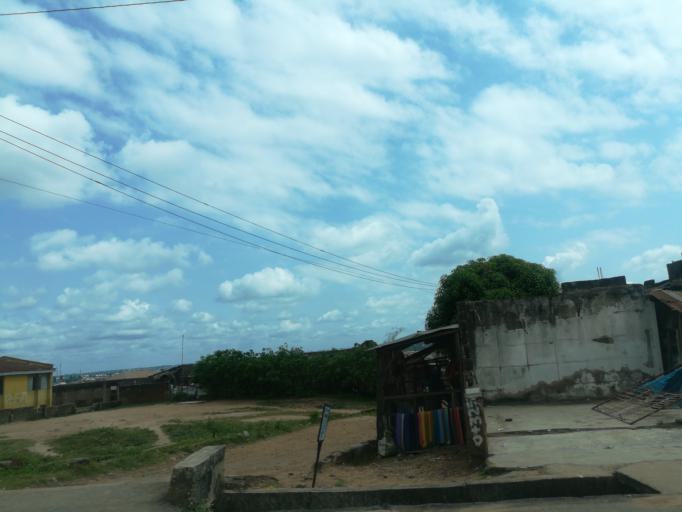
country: NG
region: Oyo
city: Egbeda
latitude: 7.4177
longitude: 4.0019
